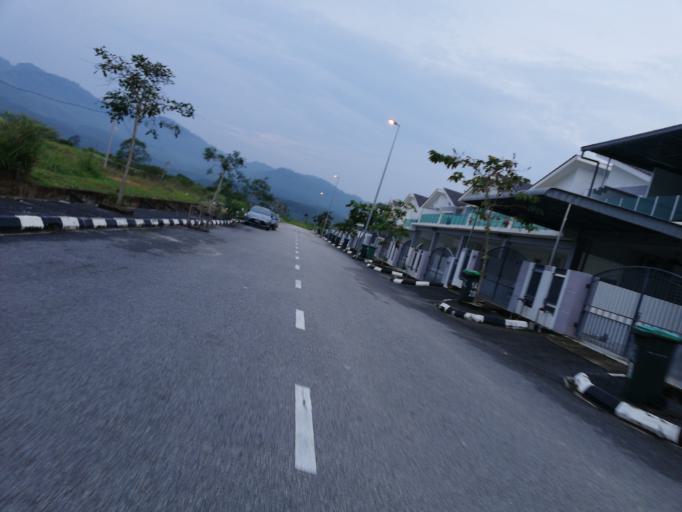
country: MY
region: Kedah
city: Kulim
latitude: 5.3855
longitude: 100.5822
